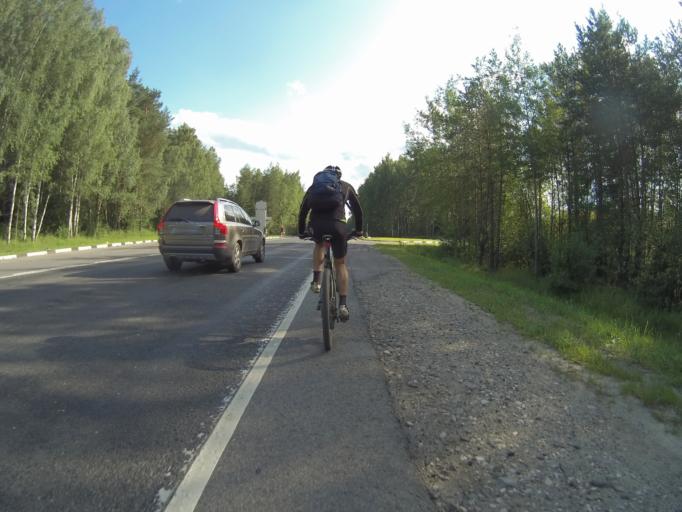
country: RU
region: Ivanovo
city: Nerl'
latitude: 56.6306
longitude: 40.5705
